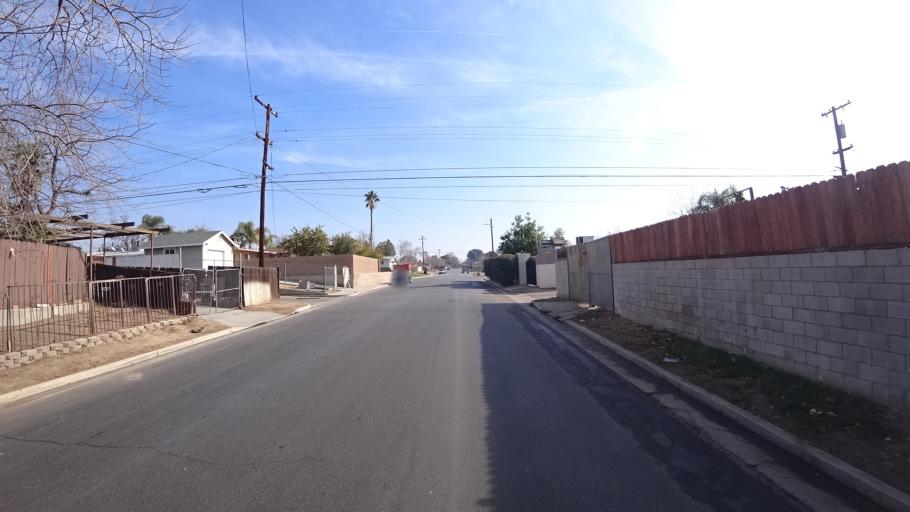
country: US
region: California
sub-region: Kern County
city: Oildale
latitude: 35.4000
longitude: -118.9703
